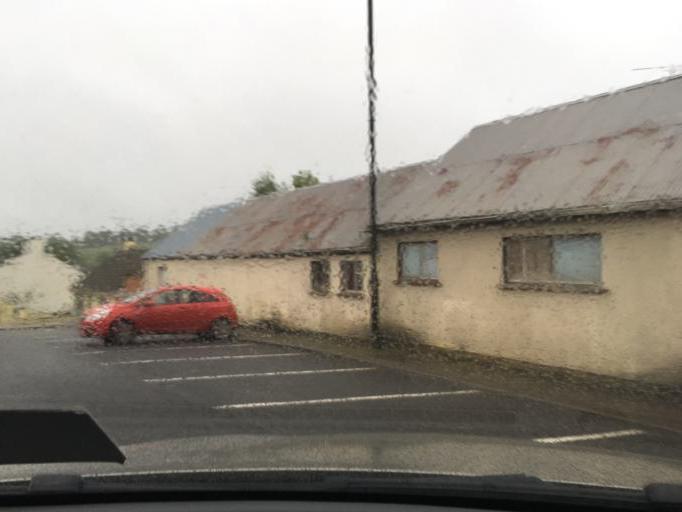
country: GB
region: Northern Ireland
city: Irvinestown
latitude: 54.5499
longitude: -7.8308
